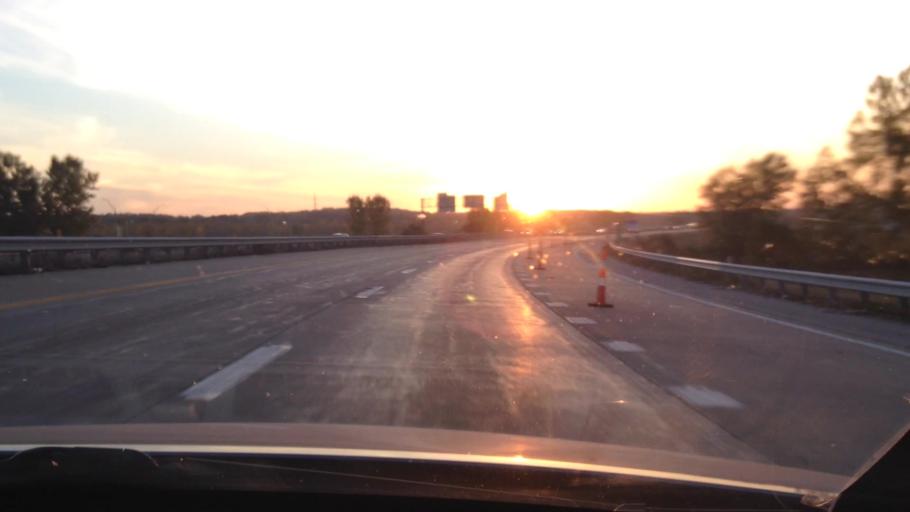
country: US
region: Missouri
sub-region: Platte County
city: Riverside
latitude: 39.1611
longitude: -94.6306
